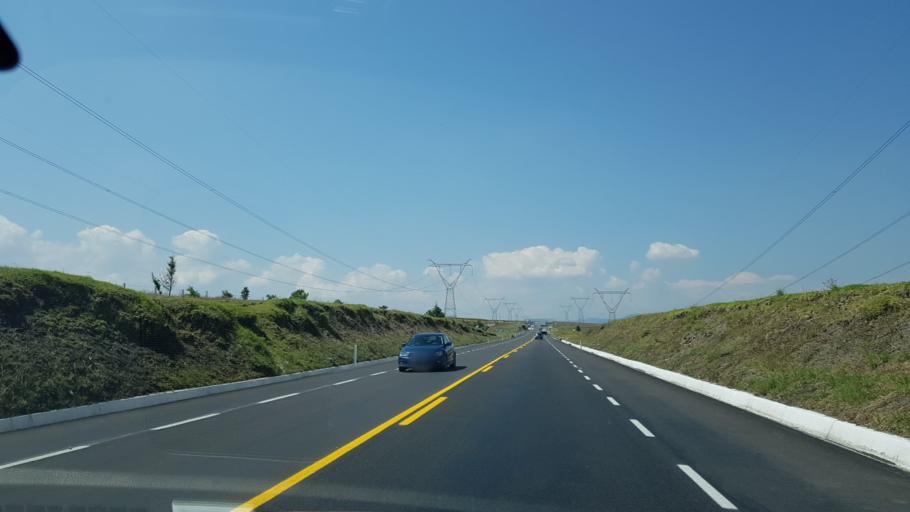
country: MX
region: Mexico
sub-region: Almoloya de Juarez
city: Conjunto Habitacional Ecologico SUTEYM
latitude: 19.3832
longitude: -99.7851
